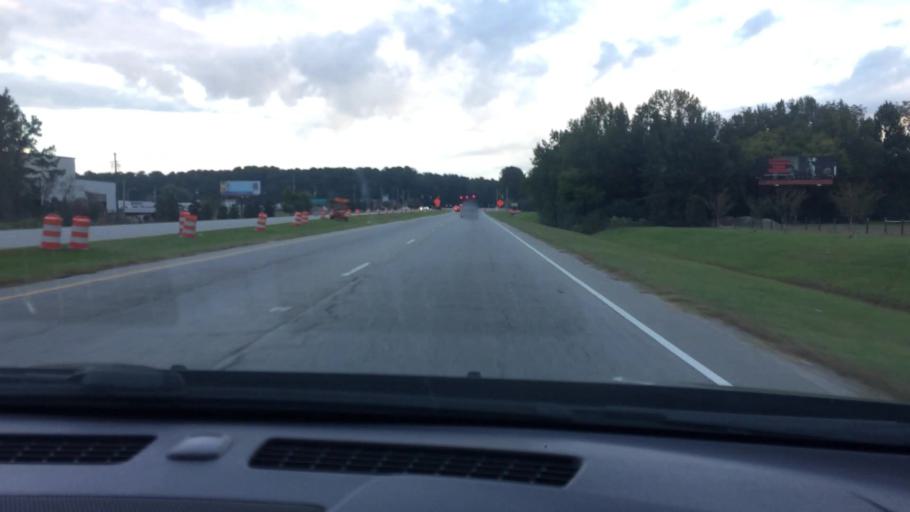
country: US
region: North Carolina
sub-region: Pitt County
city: Winterville
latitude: 35.5321
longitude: -77.4076
